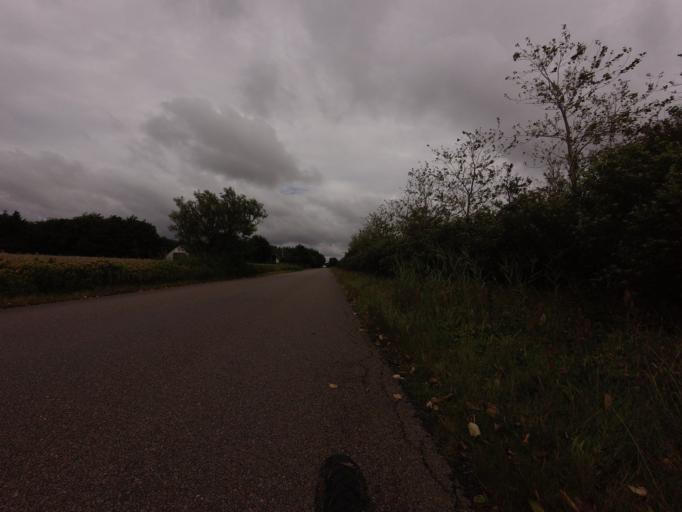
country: DK
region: North Denmark
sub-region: Jammerbugt Kommune
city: Pandrup
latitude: 57.2915
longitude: 9.7984
